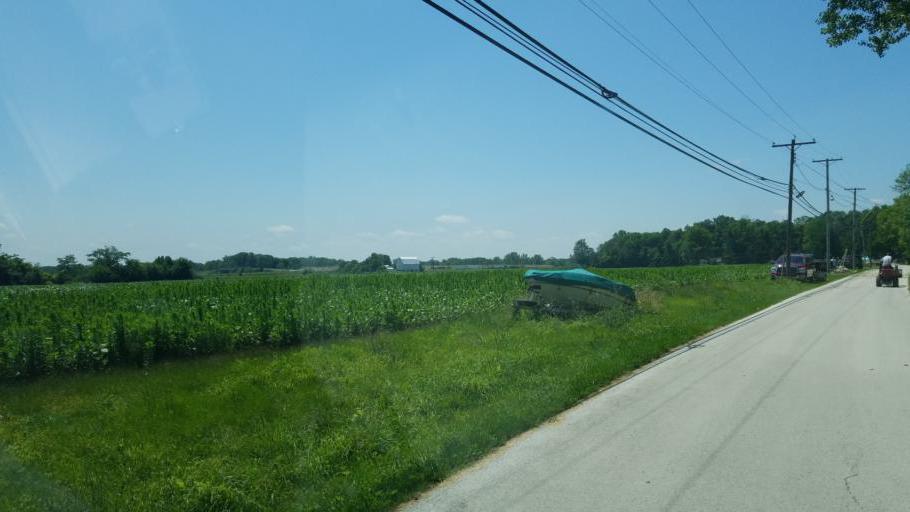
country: US
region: Ohio
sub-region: Sandusky County
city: Fremont
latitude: 41.4018
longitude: -83.0836
